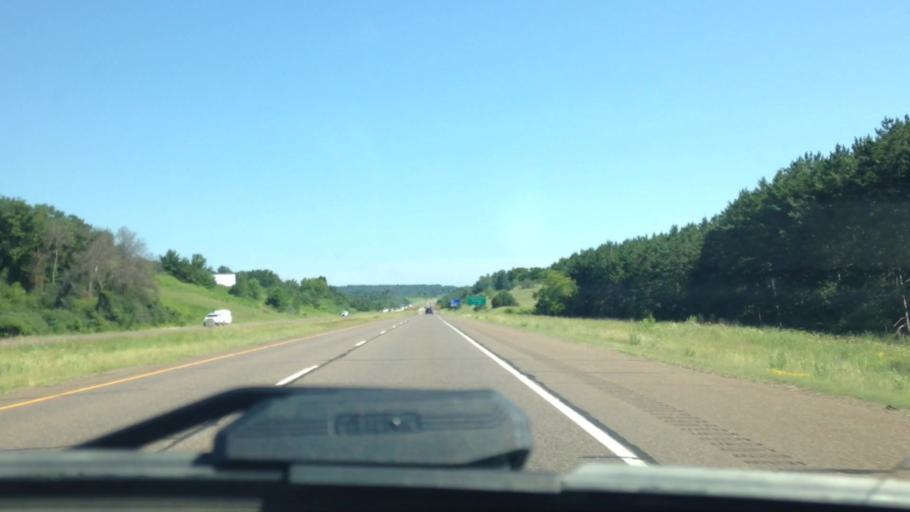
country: US
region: Wisconsin
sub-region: Chippewa County
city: Chippewa Falls
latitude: 44.9151
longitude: -91.4278
